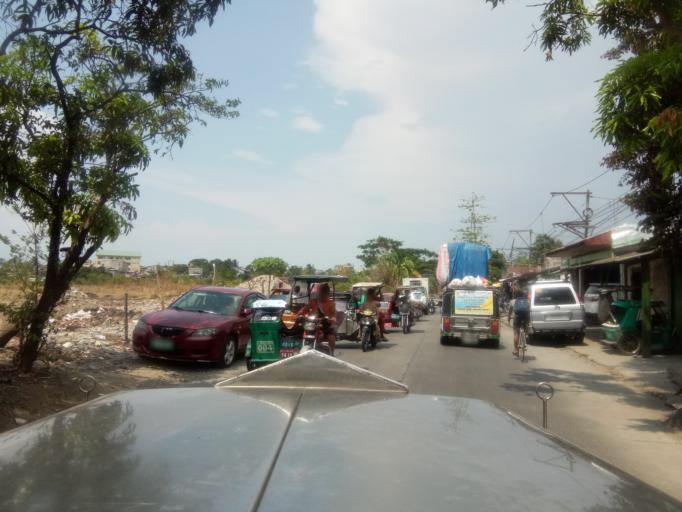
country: PH
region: Calabarzon
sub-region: Province of Cavite
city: Dasmarinas
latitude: 14.3192
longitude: 120.9764
